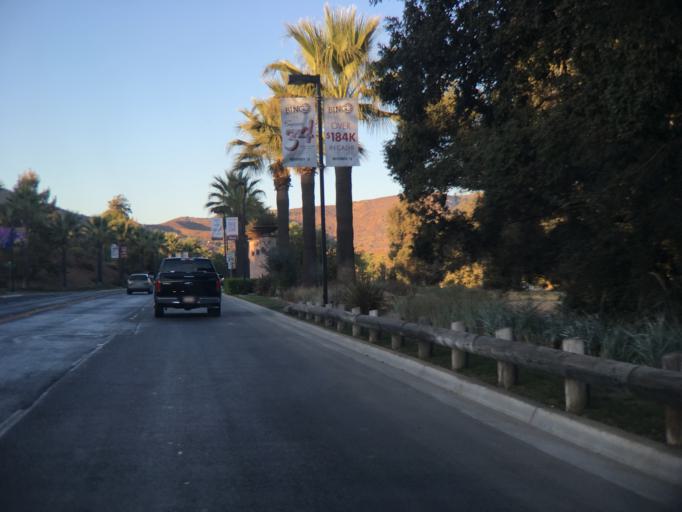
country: US
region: California
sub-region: San Diego County
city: Harbison Canyon
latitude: 32.7870
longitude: -116.8327
